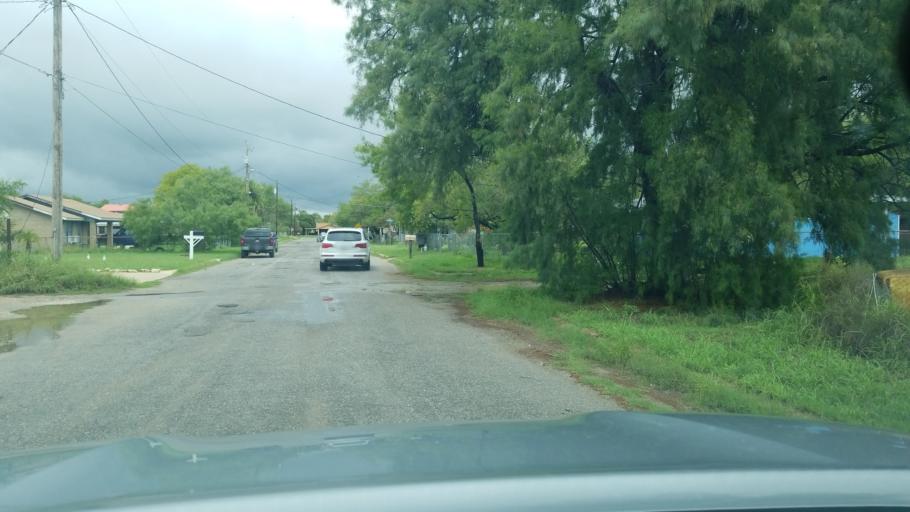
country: US
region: Texas
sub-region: Dimmit County
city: Carrizo Springs
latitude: 28.5307
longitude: -99.8486
